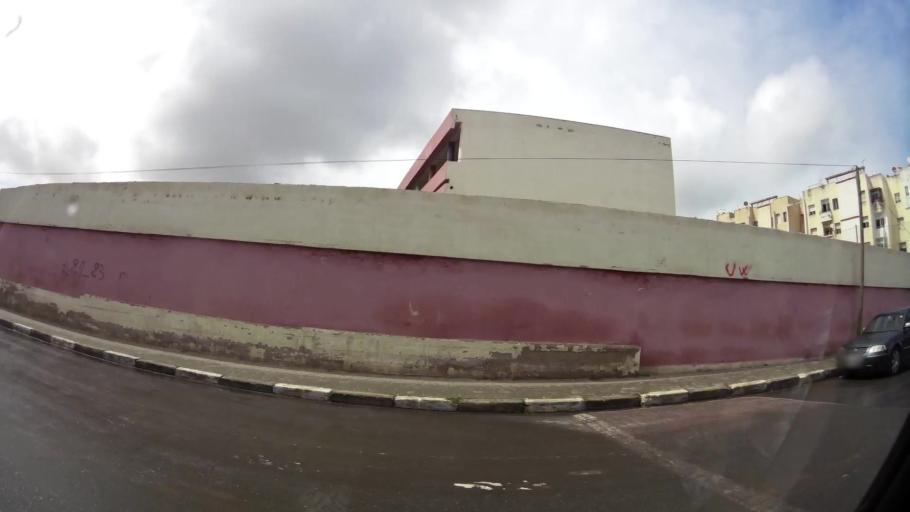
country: MA
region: Grand Casablanca
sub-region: Casablanca
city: Casablanca
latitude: 33.5242
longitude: -7.6460
